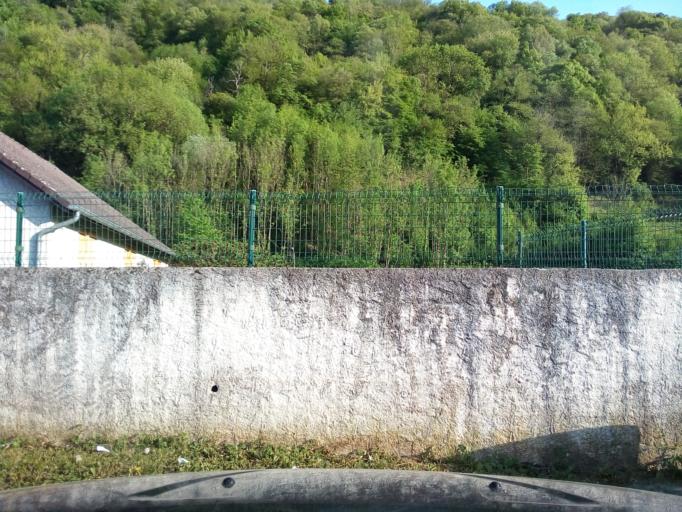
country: FR
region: Rhone-Alpes
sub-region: Departement de l'Isere
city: Gieres
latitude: 45.1869
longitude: 5.8079
